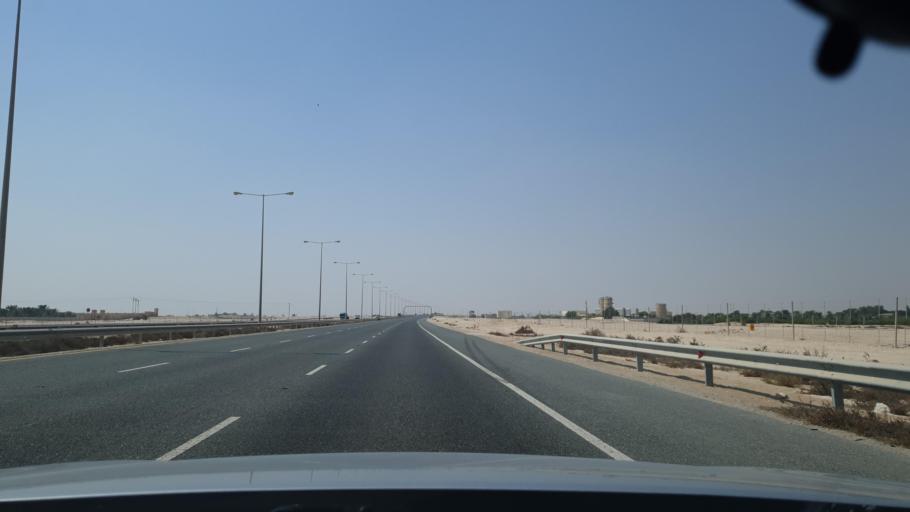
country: QA
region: Al Khawr
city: Al Khawr
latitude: 25.7548
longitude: 51.4495
